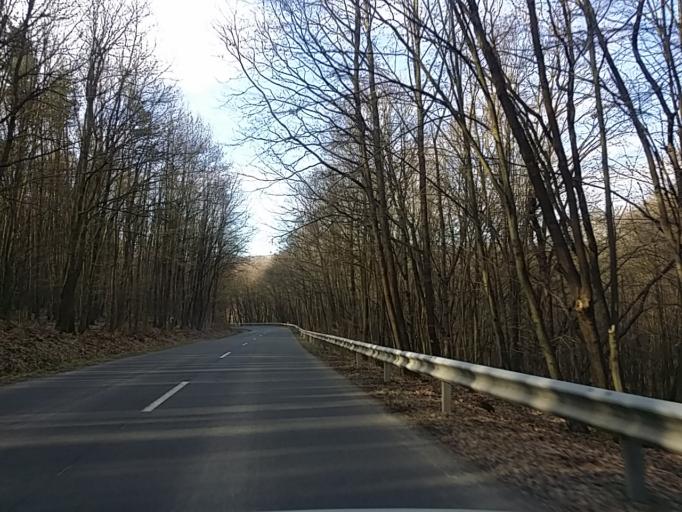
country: HU
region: Borsod-Abauj-Zemplen
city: Putnok
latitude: 48.4372
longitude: 20.4857
